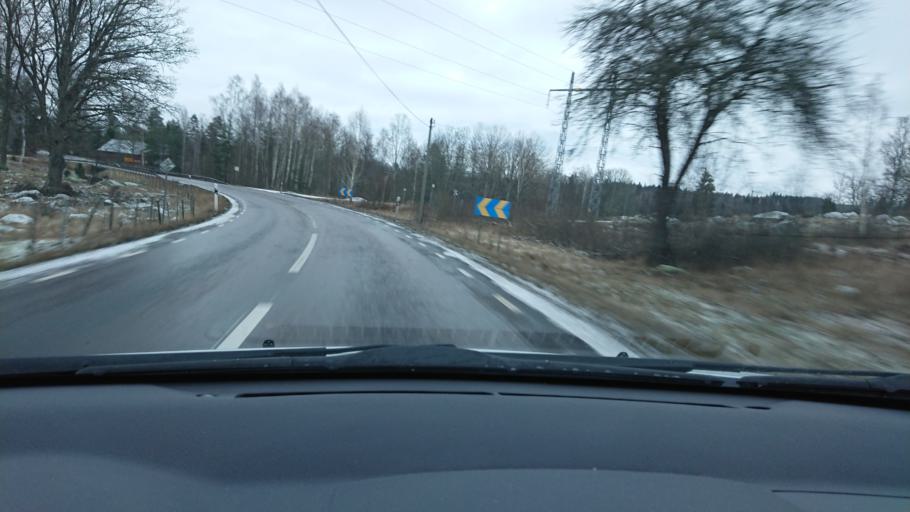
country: SE
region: Kalmar
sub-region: Hultsfreds Kommun
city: Virserum
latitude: 57.3345
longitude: 15.6000
